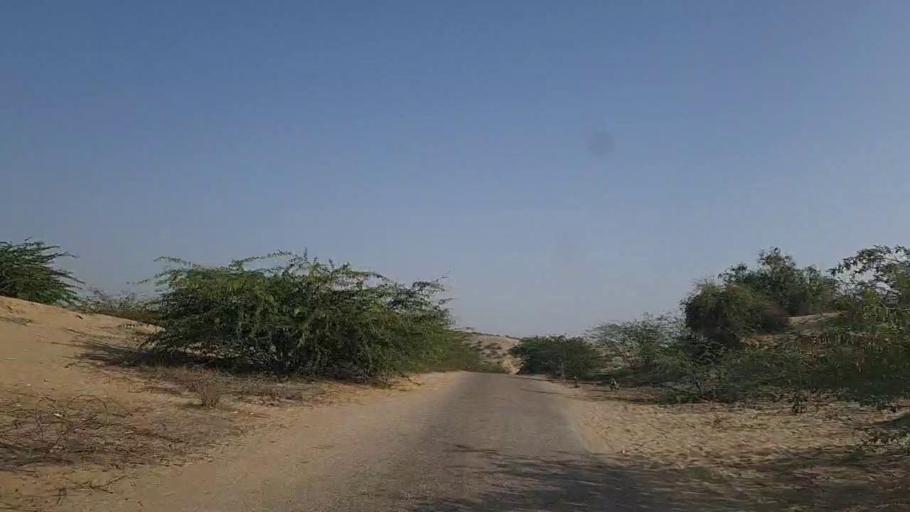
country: PK
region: Sindh
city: Naukot
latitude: 24.6240
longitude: 69.3688
